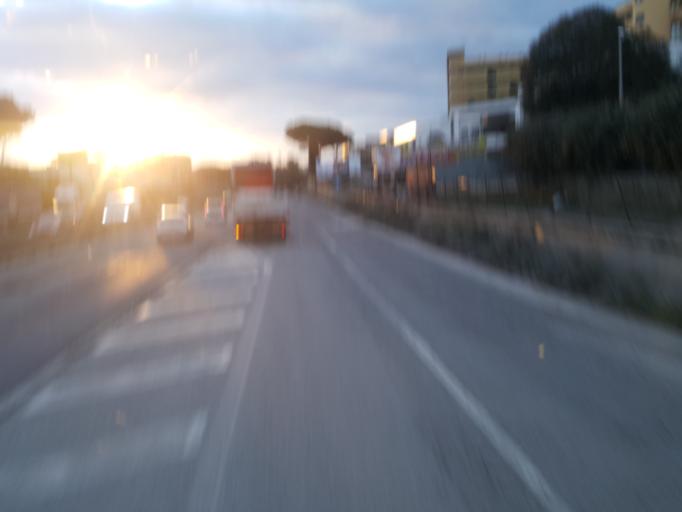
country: IT
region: Latium
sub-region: Citta metropolitana di Roma Capitale
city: Area Produttiva
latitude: 41.6866
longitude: 12.4889
